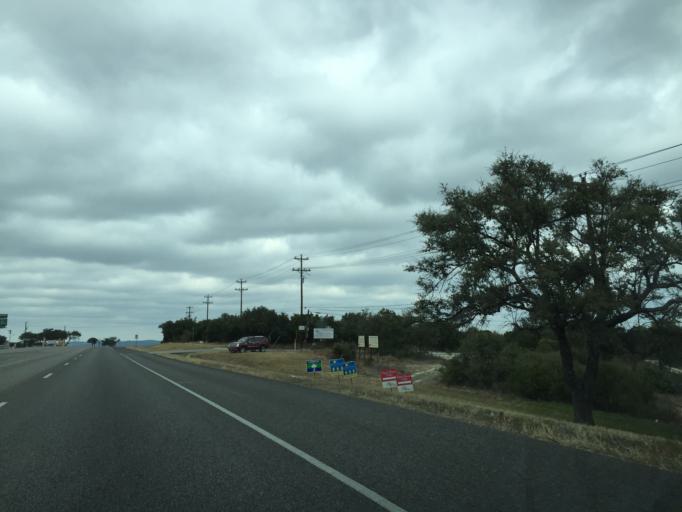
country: US
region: Texas
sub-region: Travis County
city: Briarcliff
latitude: 30.3559
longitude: -98.0668
